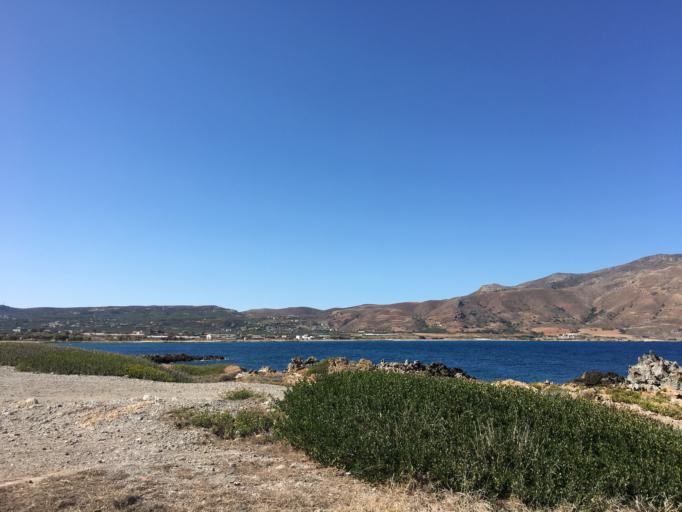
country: GR
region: Crete
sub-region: Nomos Chanias
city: Kissamos
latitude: 35.5182
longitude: 23.6366
